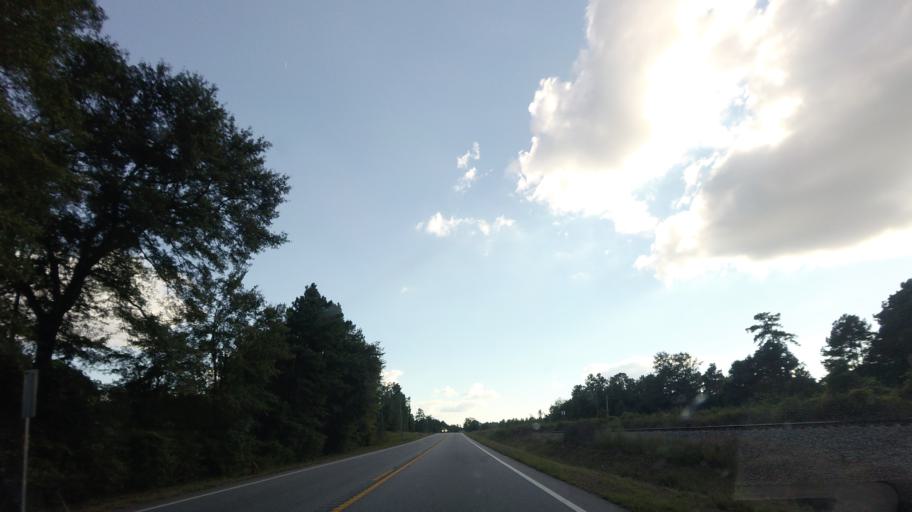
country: US
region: Georgia
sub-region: Lamar County
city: Barnesville
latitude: 33.0117
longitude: -84.1884
